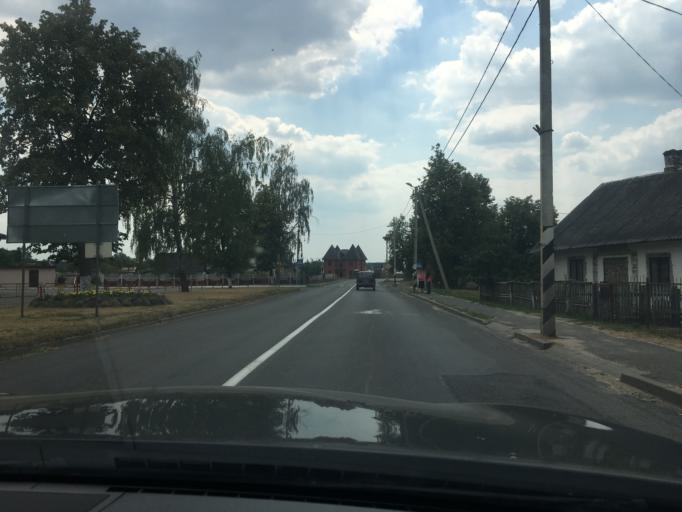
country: BY
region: Brest
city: Ruzhany
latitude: 52.8608
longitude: 24.8907
